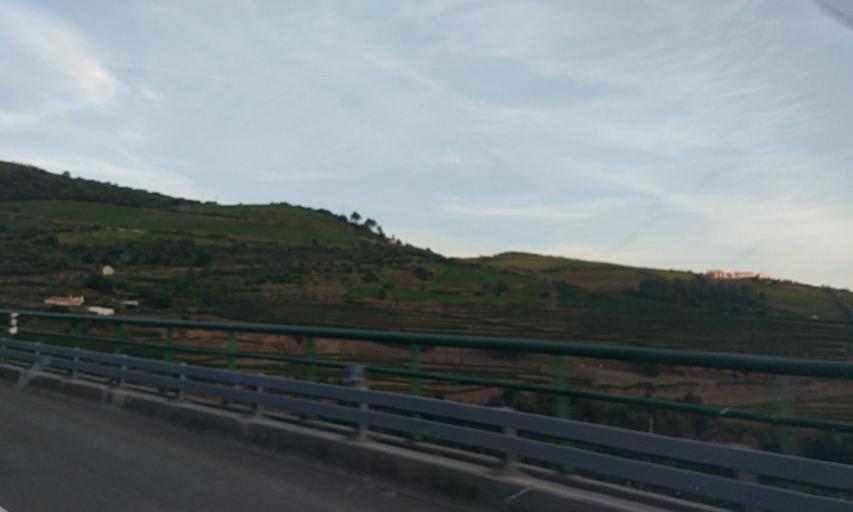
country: PT
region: Vila Real
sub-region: Peso da Regua
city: Peso da Regua
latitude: 41.1718
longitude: -7.7567
